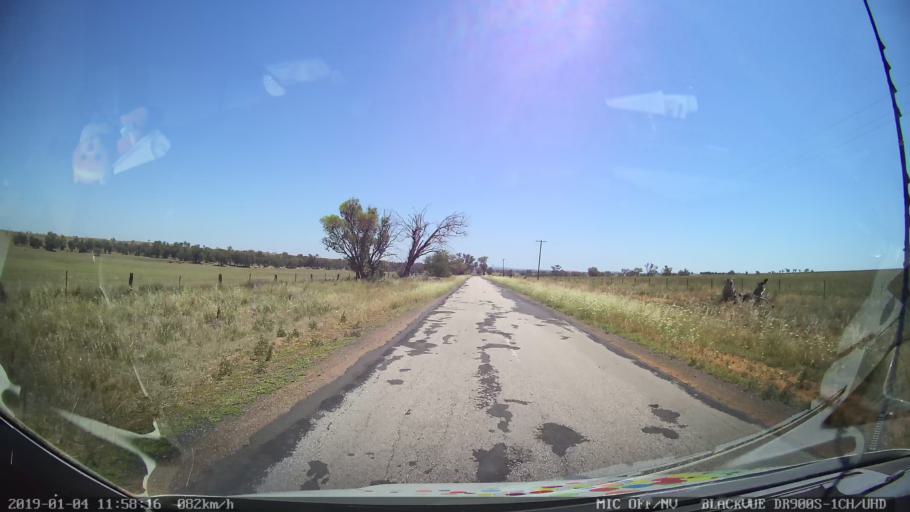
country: AU
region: New South Wales
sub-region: Cabonne
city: Molong
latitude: -32.8266
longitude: 148.7021
